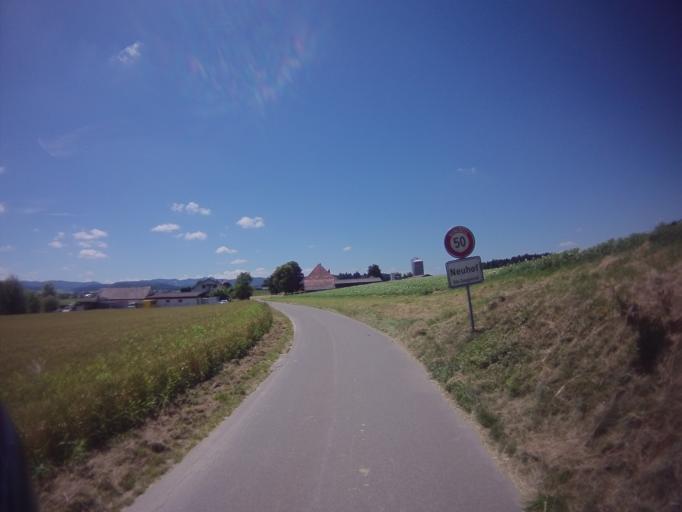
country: CH
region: Bern
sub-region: Emmental District
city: Hindelbank
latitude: 47.0637
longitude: 7.5370
